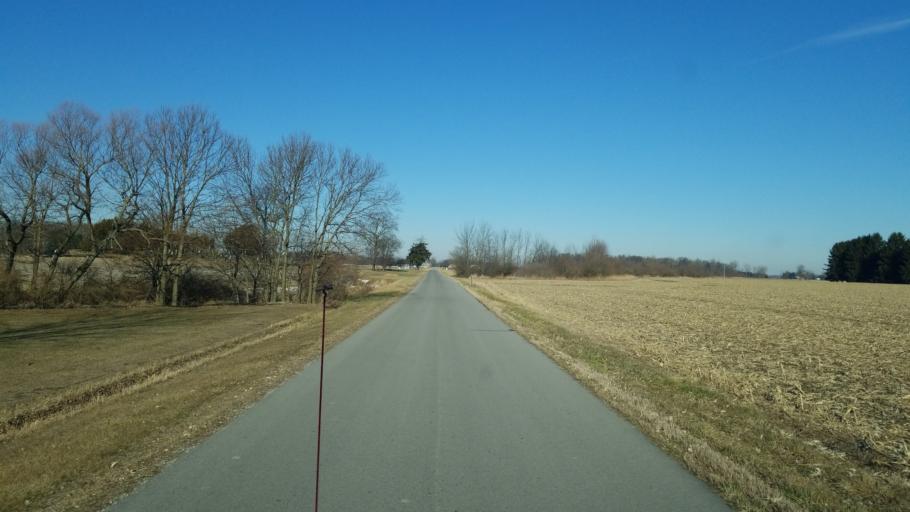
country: US
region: Ohio
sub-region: Henry County
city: Liberty Center
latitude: 41.3814
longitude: -83.9706
